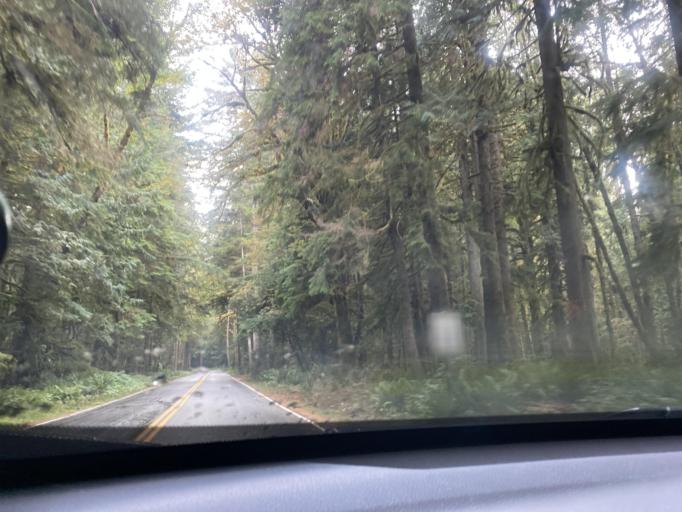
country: CA
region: British Columbia
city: Sooke
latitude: 48.0577
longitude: -123.7922
